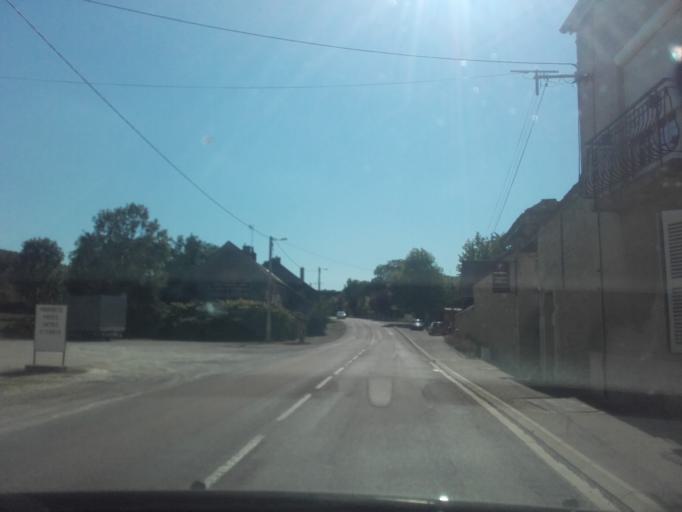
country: FR
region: Bourgogne
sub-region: Departement de la Cote-d'Or
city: Nolay
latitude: 46.9550
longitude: 4.6750
